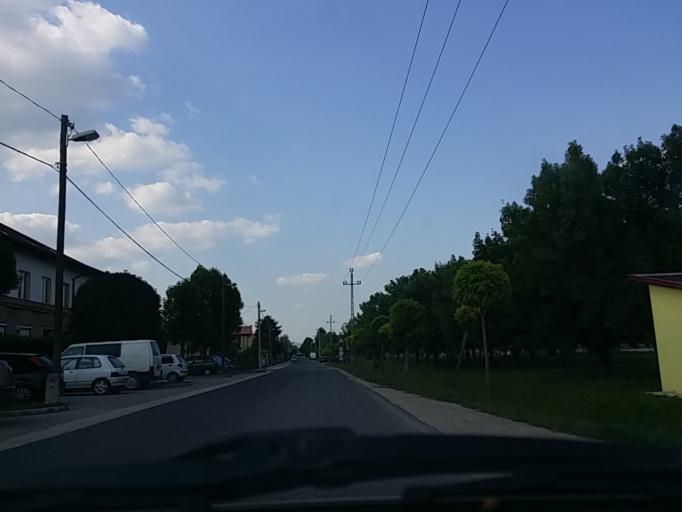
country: HU
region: Pest
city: Budakalasz
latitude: 47.6172
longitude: 19.0585
